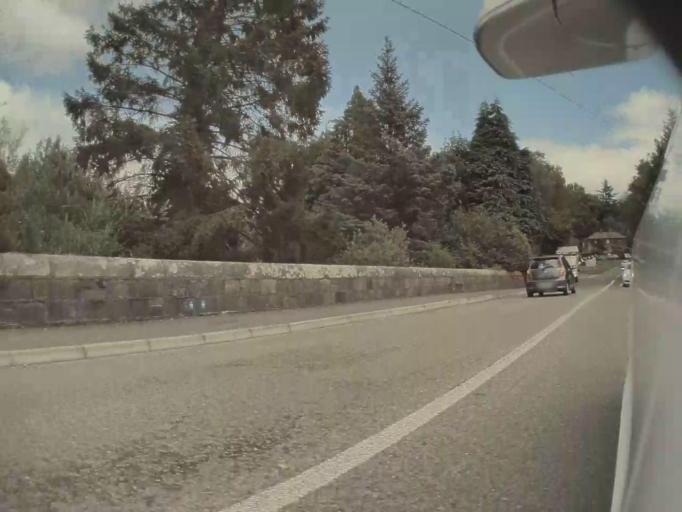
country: IE
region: Leinster
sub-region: Wicklow
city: Rathdrum
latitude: 53.0082
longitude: -6.2987
